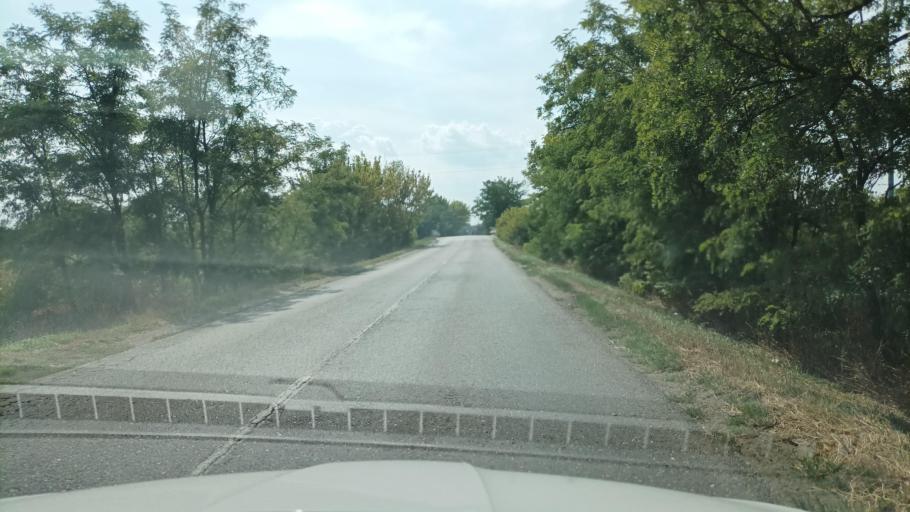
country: HU
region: Pest
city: Tura
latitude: 47.6147
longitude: 19.6071
